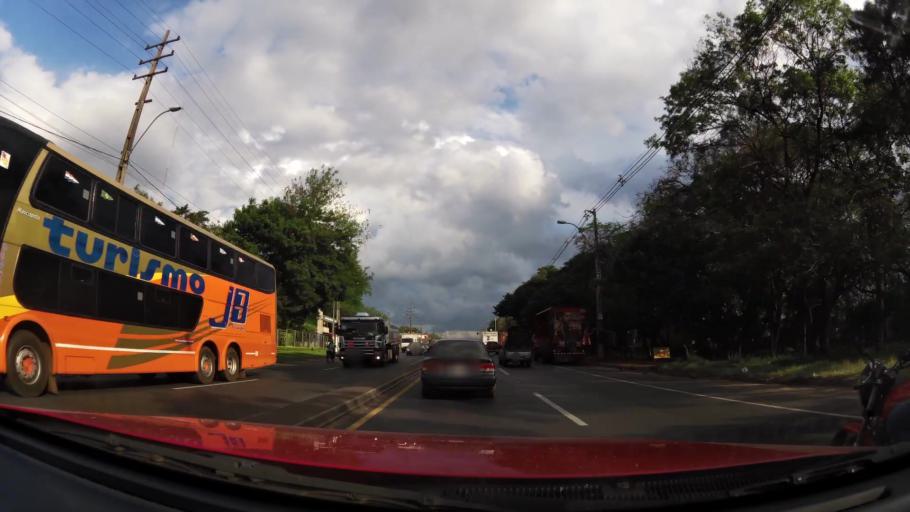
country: PY
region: Central
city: Villa Elisa
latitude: -25.3638
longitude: -57.5648
